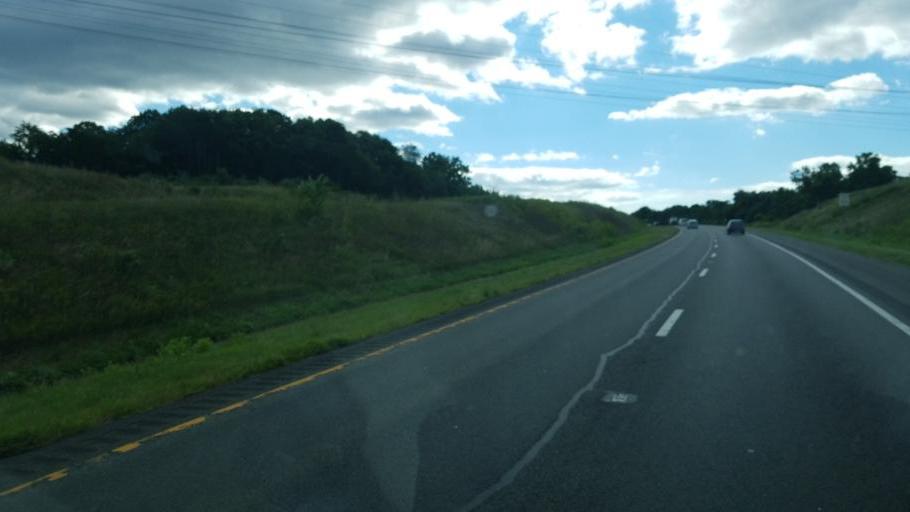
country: US
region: Virginia
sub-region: Warren County
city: Front Royal
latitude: 38.9530
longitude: -78.1811
